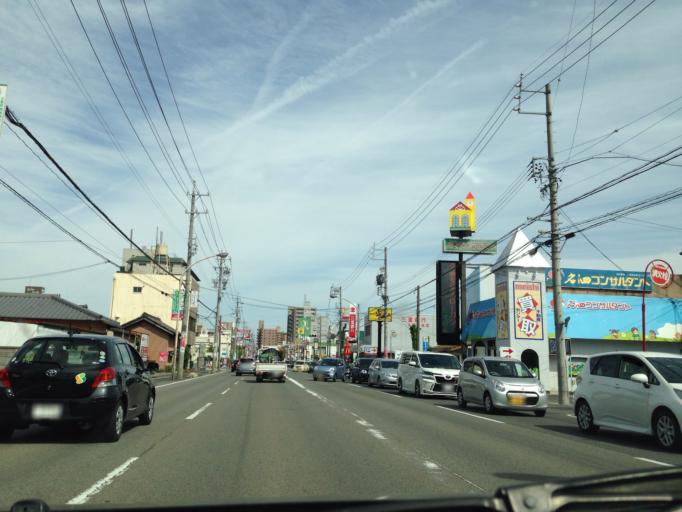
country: JP
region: Mie
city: Yokkaichi
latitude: 34.9749
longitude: 136.6065
